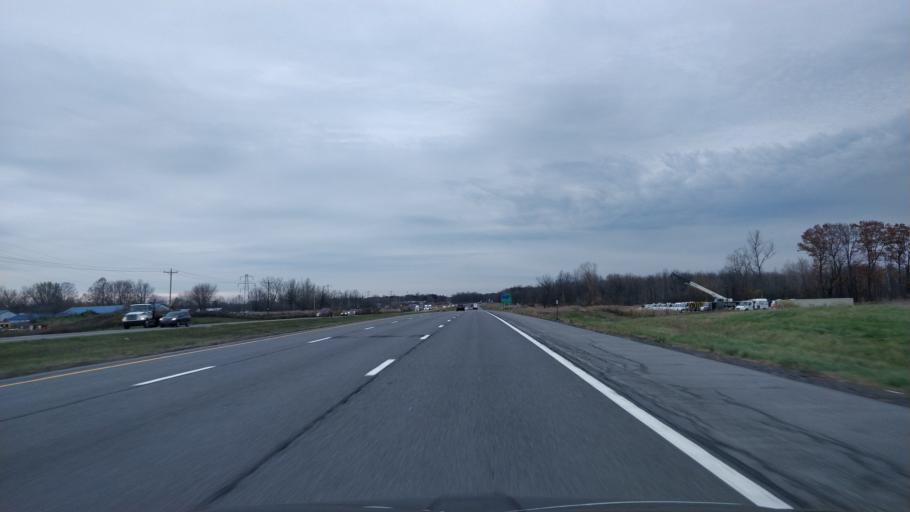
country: US
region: New York
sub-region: Onondaga County
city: Brewerton
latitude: 43.2003
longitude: -76.1249
